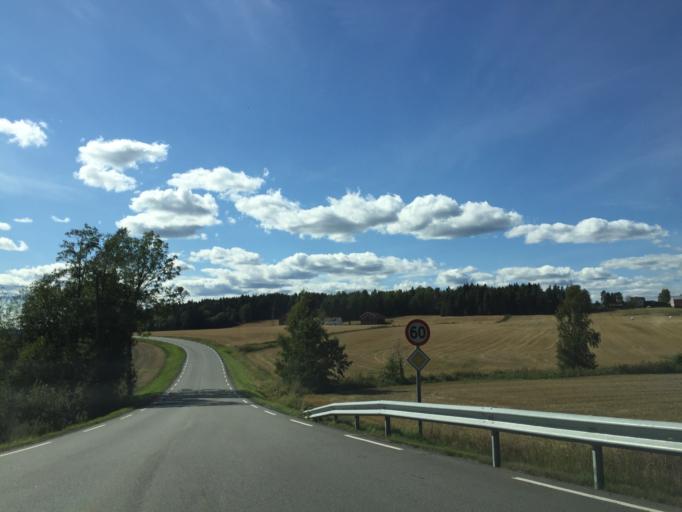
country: NO
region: Buskerud
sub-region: Ovre Eiker
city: Hokksund
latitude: 59.7067
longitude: 9.8627
